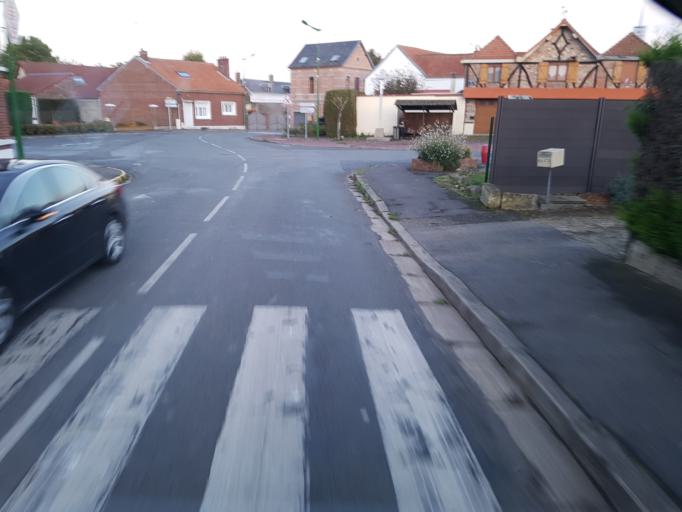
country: FR
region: Picardie
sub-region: Departement de la Somme
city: Sains-en-Amienois
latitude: 49.7679
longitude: 2.2703
